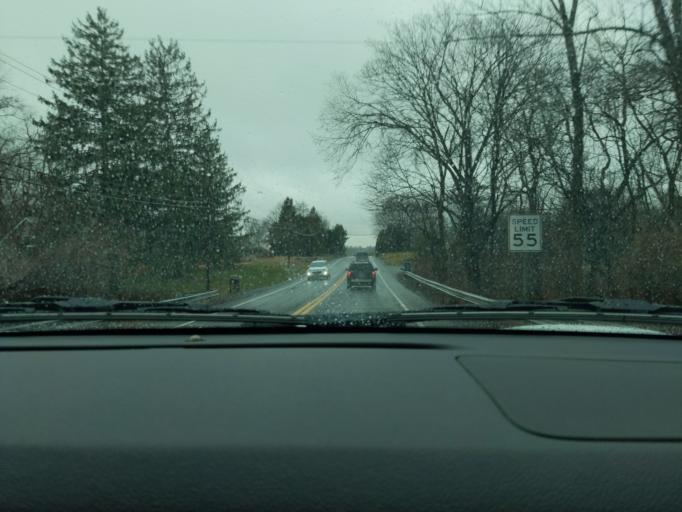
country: US
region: Pennsylvania
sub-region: Bucks County
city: Perkasie
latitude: 40.4096
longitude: -75.2629
